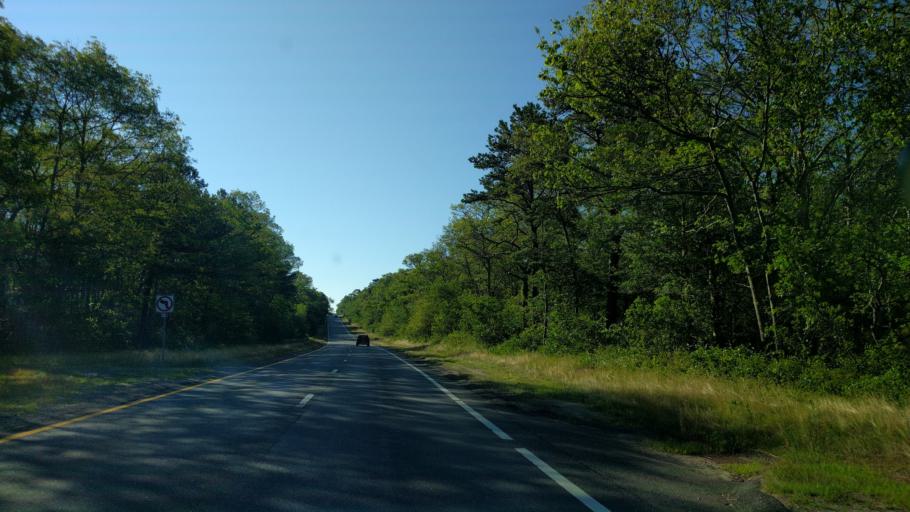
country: US
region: Massachusetts
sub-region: Barnstable County
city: West Barnstable
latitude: 41.6903
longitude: -70.3744
